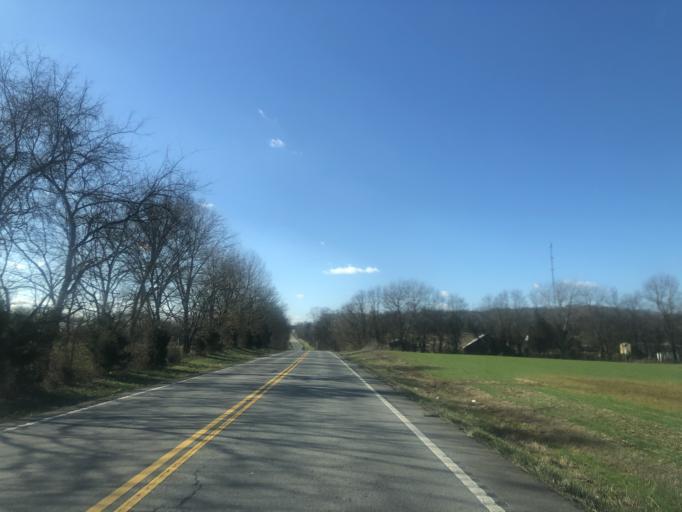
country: US
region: Tennessee
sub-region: Williamson County
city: Nolensville
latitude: 35.8525
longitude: -86.6386
